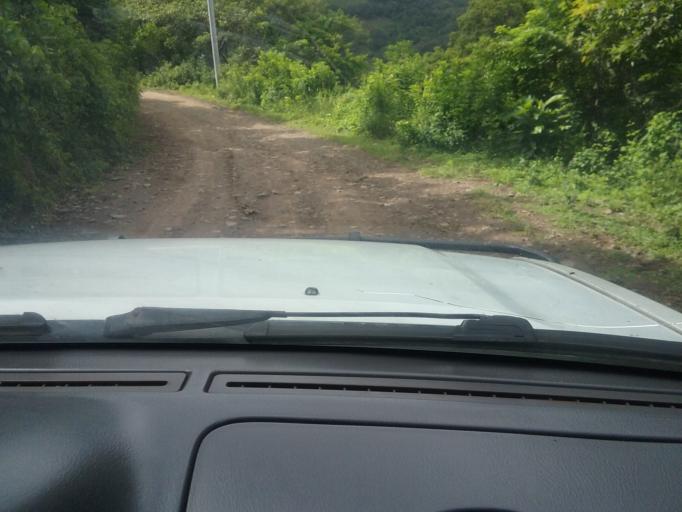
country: NI
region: Matagalpa
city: Matagalpa
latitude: 12.8716
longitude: -85.9551
